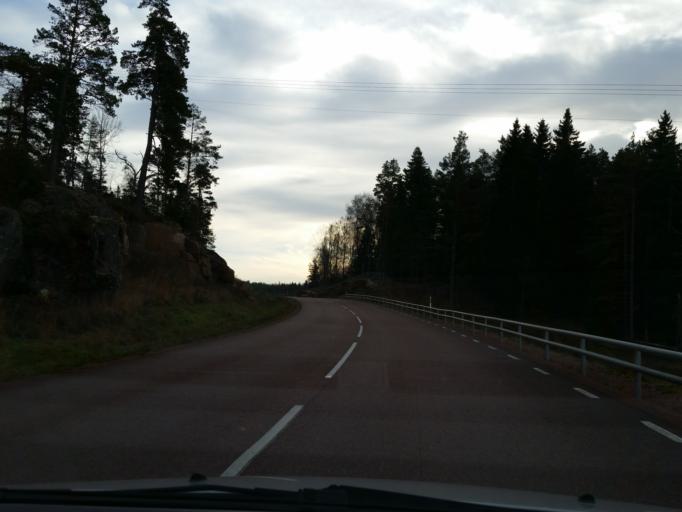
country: AX
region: Alands landsbygd
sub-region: Saltvik
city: Saltvik
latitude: 60.2491
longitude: 20.0396
